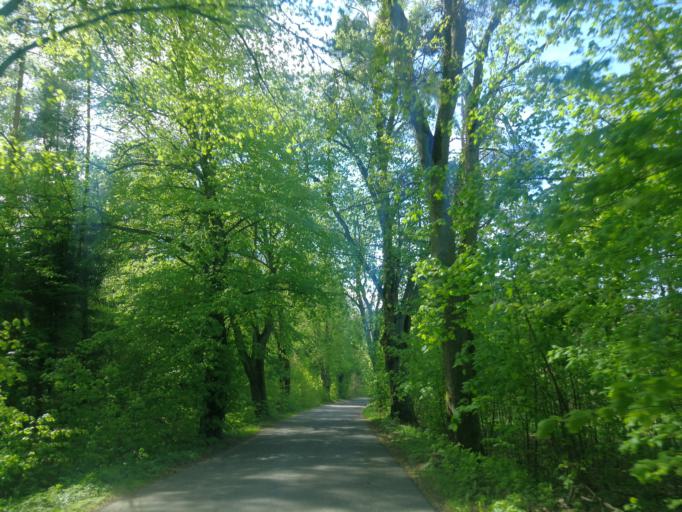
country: PL
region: Warmian-Masurian Voivodeship
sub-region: Powiat ilawski
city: Zalewo
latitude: 53.7077
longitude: 19.6854
